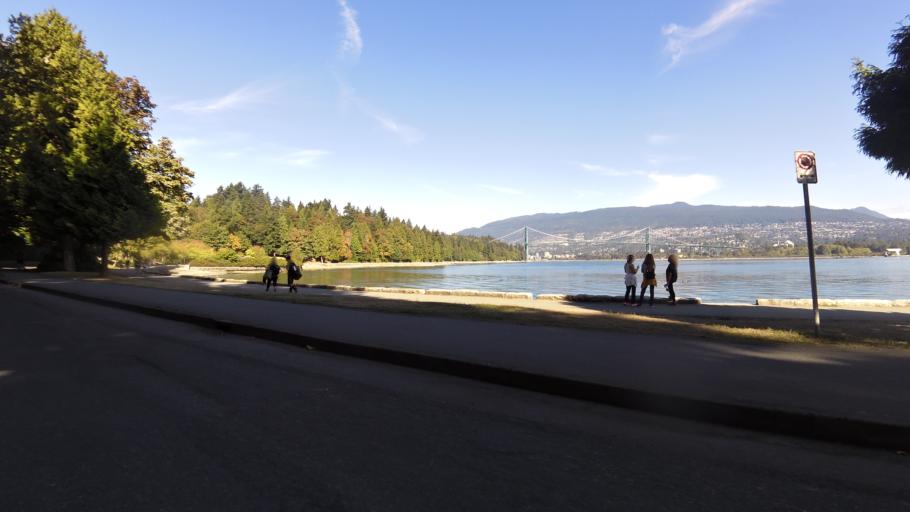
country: CA
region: British Columbia
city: West End
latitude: 49.3025
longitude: -123.1270
